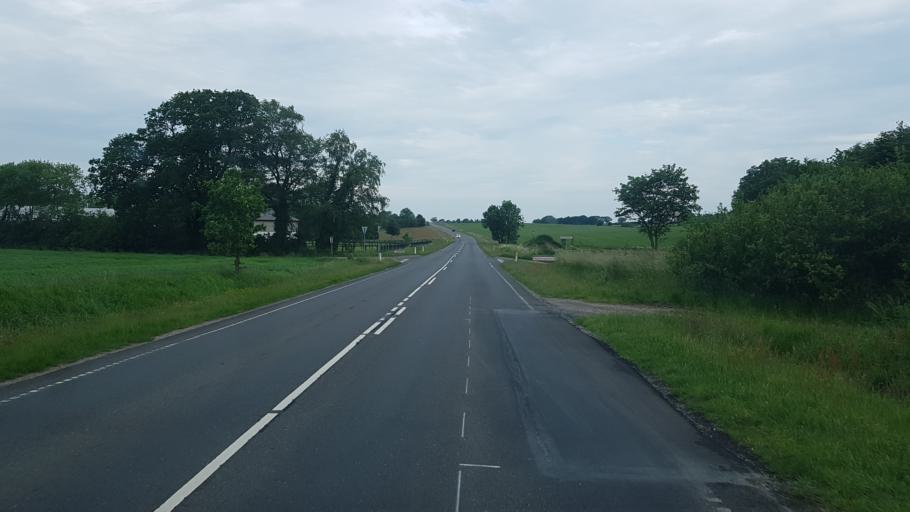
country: DK
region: South Denmark
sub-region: Vejen Kommune
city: Rodding
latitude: 55.3934
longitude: 9.0401
